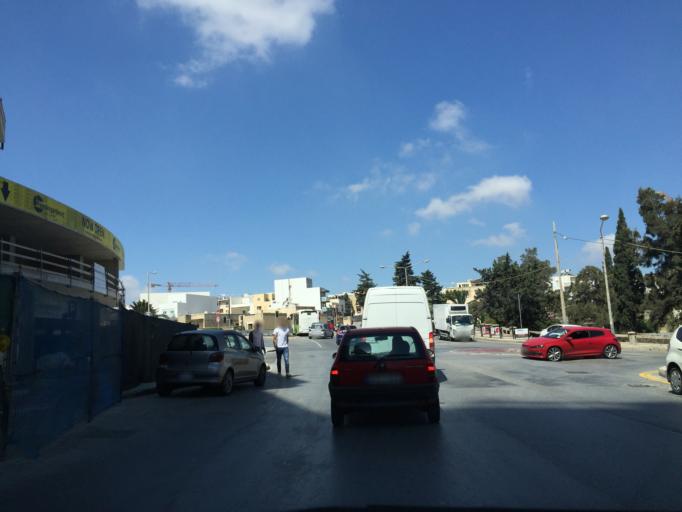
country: MT
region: Saint Julian
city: San Giljan
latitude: 35.9223
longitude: 14.4877
